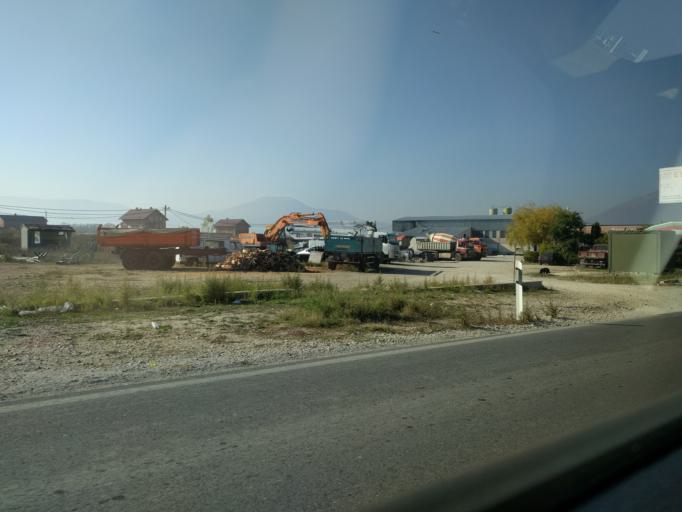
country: XK
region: Prizren
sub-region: Prizren
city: Prizren
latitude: 42.2490
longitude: 20.7320
